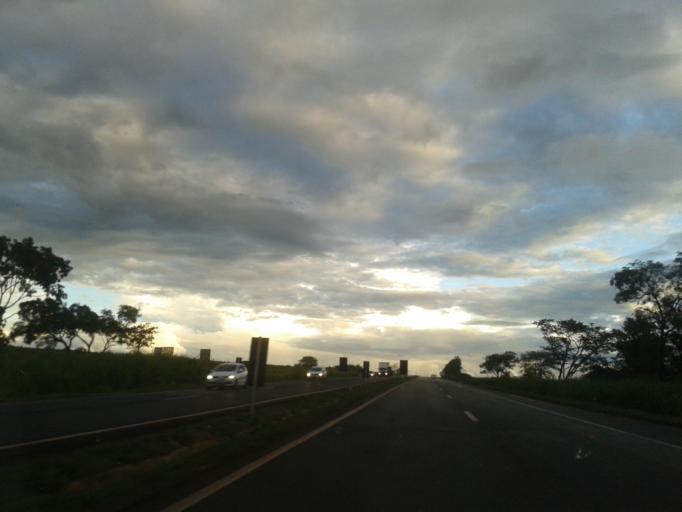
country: BR
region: Minas Gerais
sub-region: Centralina
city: Centralina
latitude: -18.6313
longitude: -49.1836
